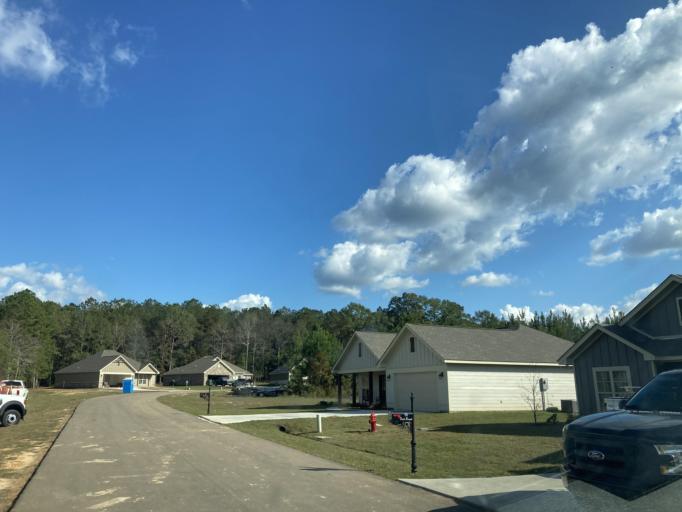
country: US
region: Mississippi
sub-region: Lamar County
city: Sumrall
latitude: 31.4301
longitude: -89.5335
